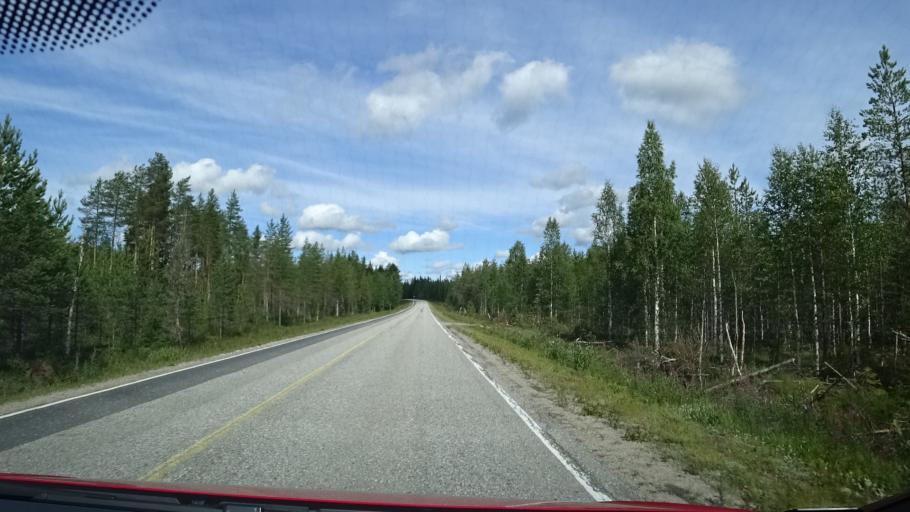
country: FI
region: Kainuu
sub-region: Kehys-Kainuu
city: Kuhmo
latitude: 64.4730
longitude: 29.7440
